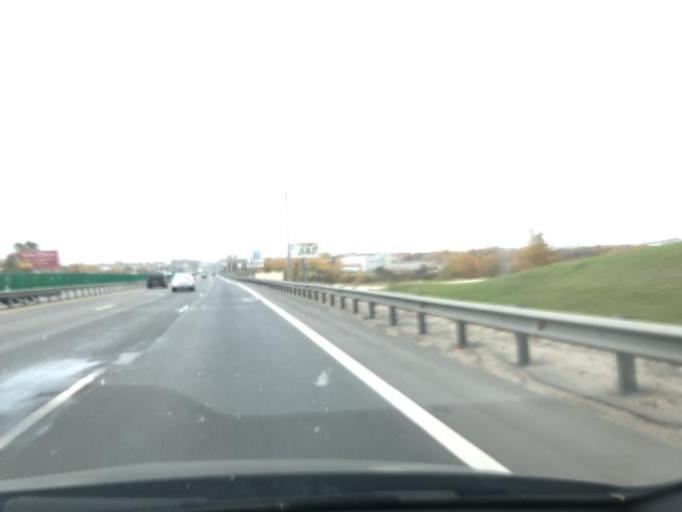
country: BY
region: Minsk
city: Vyaliki Trastsyanets
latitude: 53.8416
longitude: 27.6641
